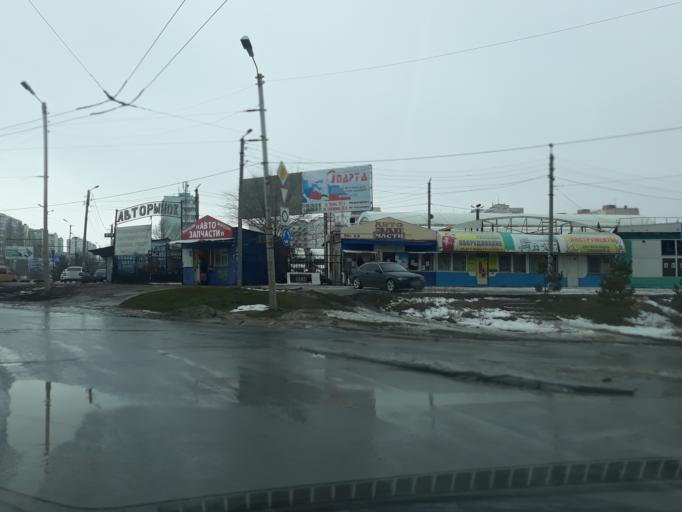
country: RU
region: Rostov
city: Novobessergenovka
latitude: 47.2197
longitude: 38.8612
